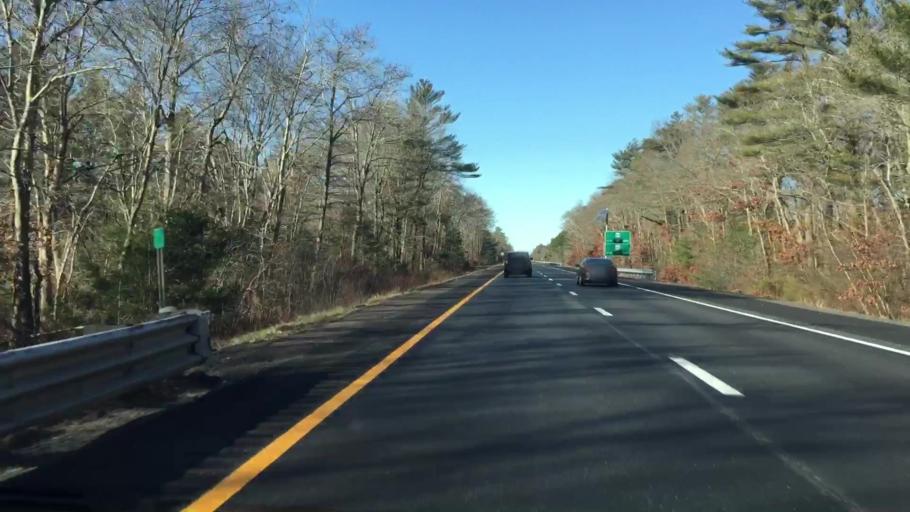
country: US
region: Massachusetts
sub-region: Plymouth County
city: West Wareham
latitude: 41.8186
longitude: -70.8008
